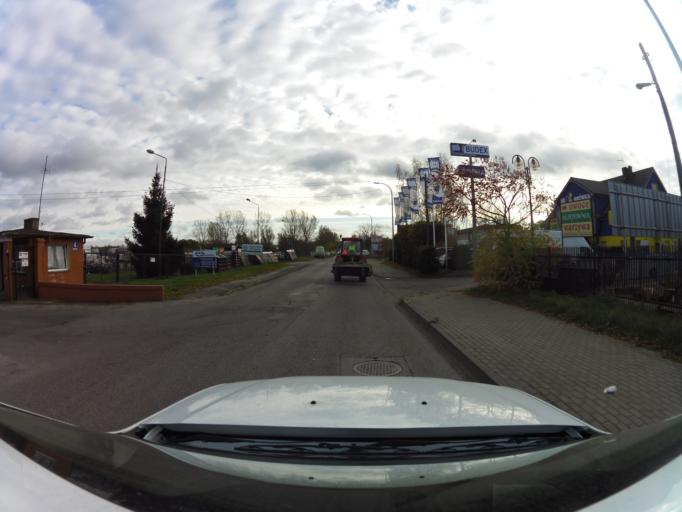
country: PL
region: West Pomeranian Voivodeship
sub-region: Powiat gryficki
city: Gryfice
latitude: 53.9270
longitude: 15.1948
